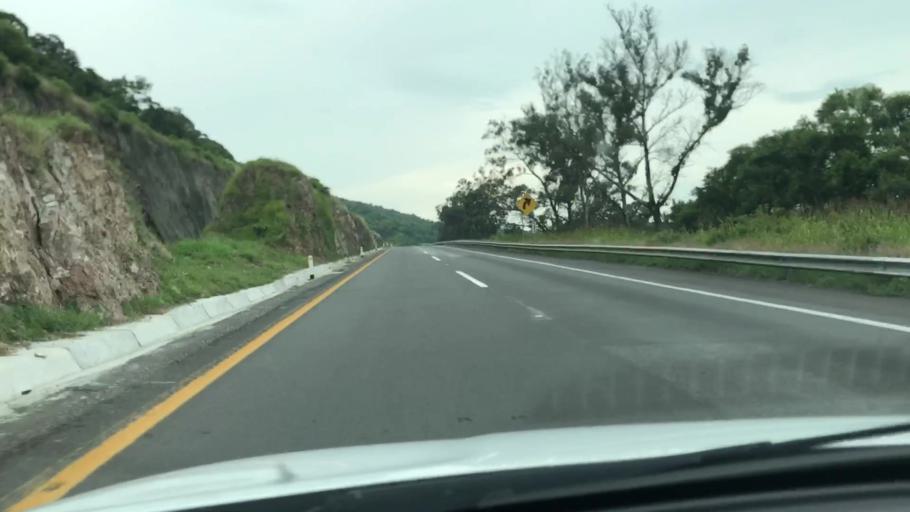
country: MX
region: Jalisco
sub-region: Zapotlan del Rey
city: Zapotlan del Rey
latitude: 20.5011
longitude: -102.9519
